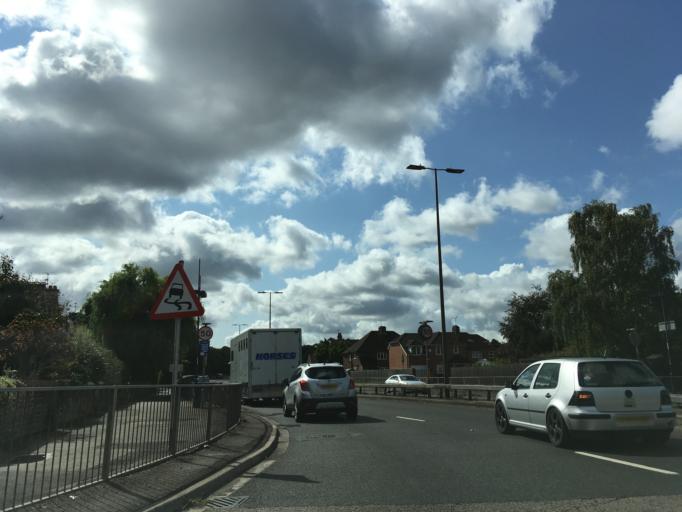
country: GB
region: England
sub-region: West Berkshire
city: Newbury
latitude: 51.3961
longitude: -1.3200
